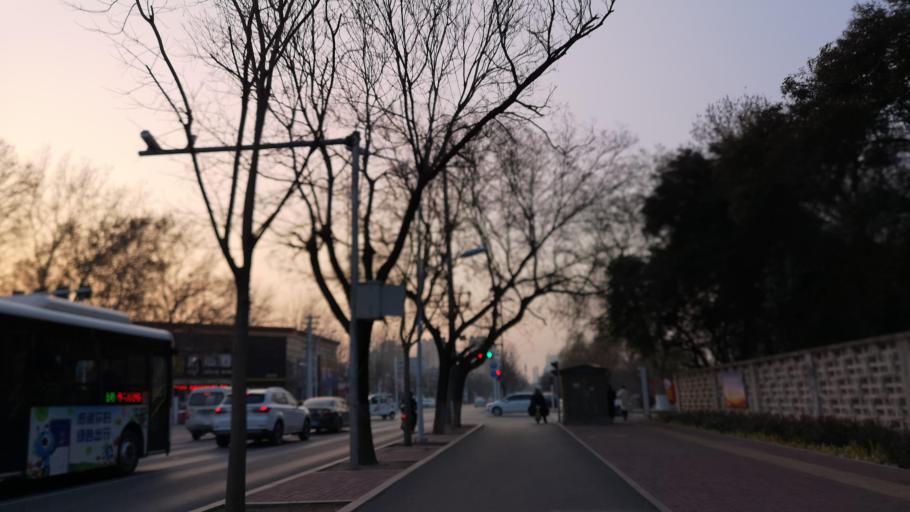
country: CN
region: Henan Sheng
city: Zhongyuanlu
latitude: 35.7723
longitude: 115.0759
